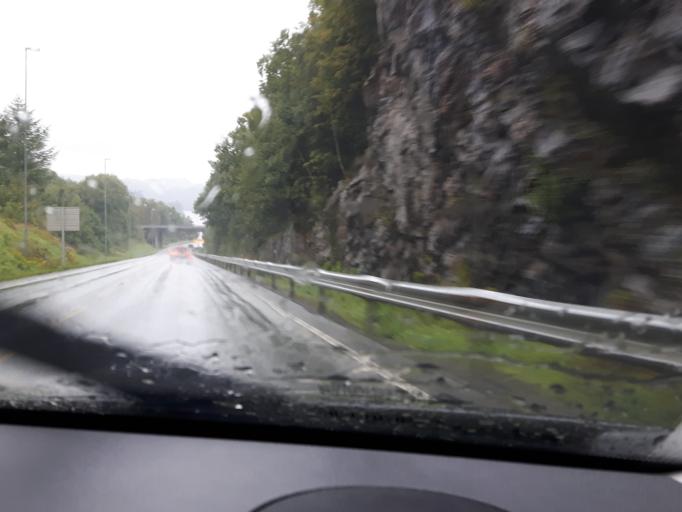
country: NO
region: Vest-Agder
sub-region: Mandal
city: Mandal
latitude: 58.0344
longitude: 7.4528
